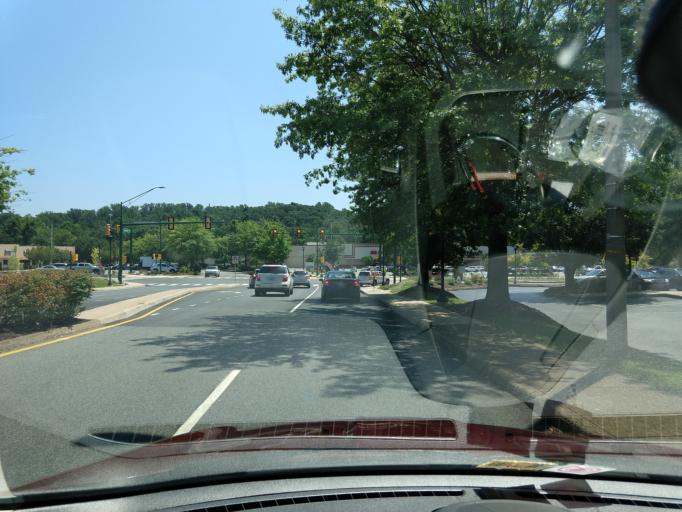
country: US
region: Virginia
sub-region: City of Charlottesville
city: Charlottesville
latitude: 38.0652
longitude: -78.4873
